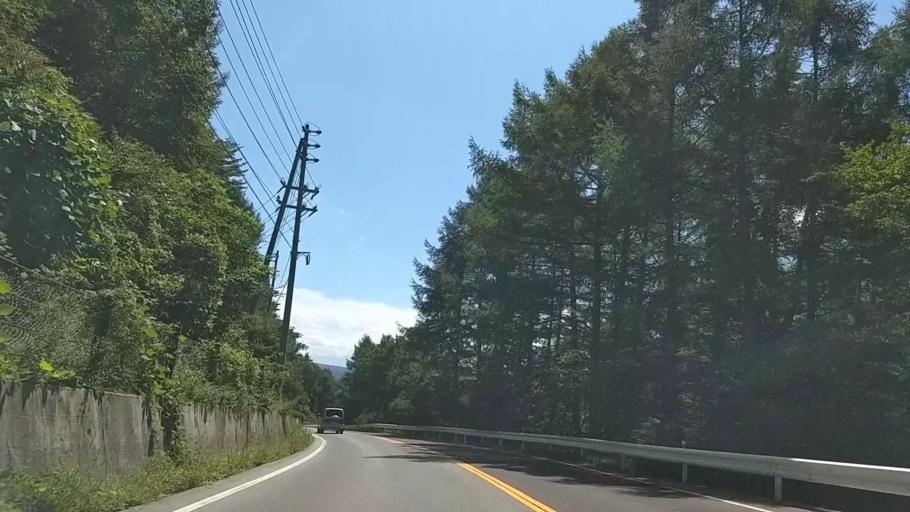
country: JP
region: Nagano
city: Chino
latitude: 36.0764
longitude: 138.2221
